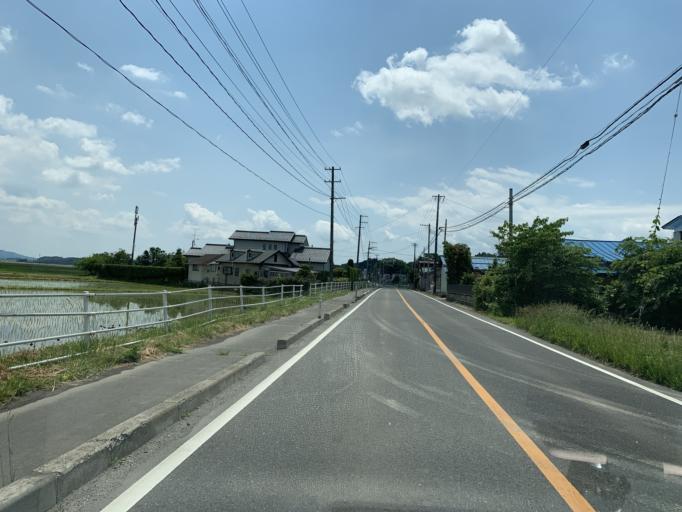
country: JP
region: Miyagi
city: Kogota
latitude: 38.5091
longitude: 141.0686
